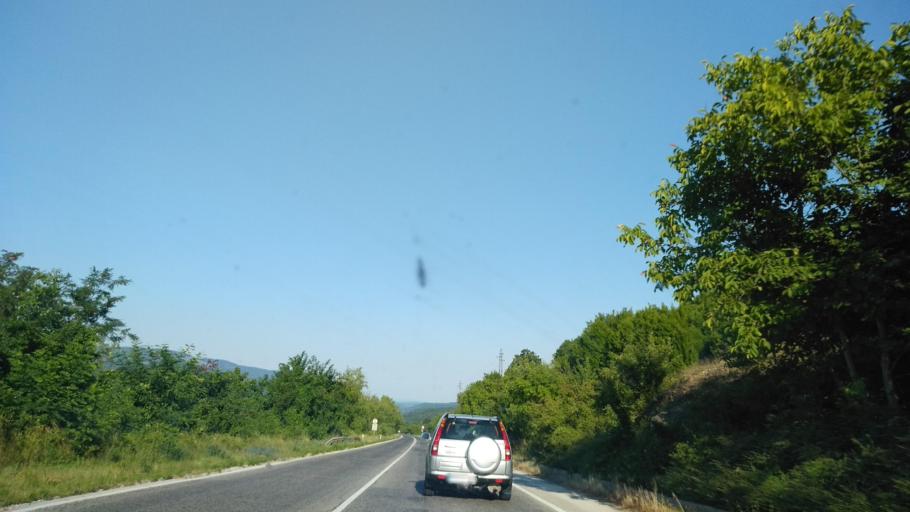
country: BG
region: Lovech
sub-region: Obshtina Lovech
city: Lovech
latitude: 43.0480
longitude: 24.7764
